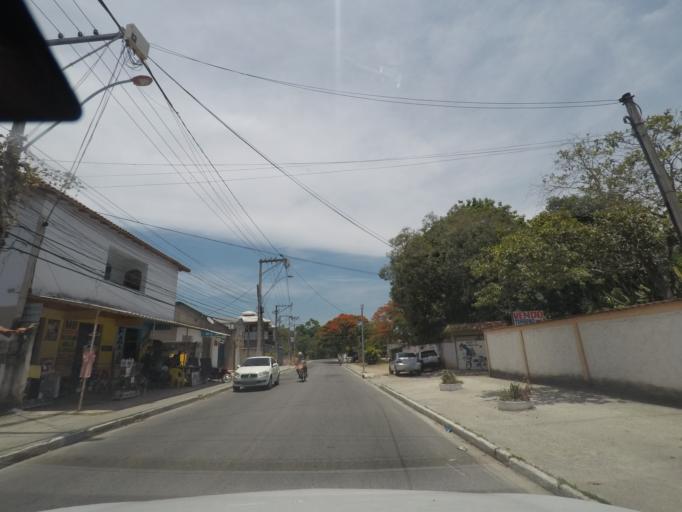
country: BR
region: Rio de Janeiro
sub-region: Marica
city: Marica
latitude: -22.9127
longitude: -42.8221
